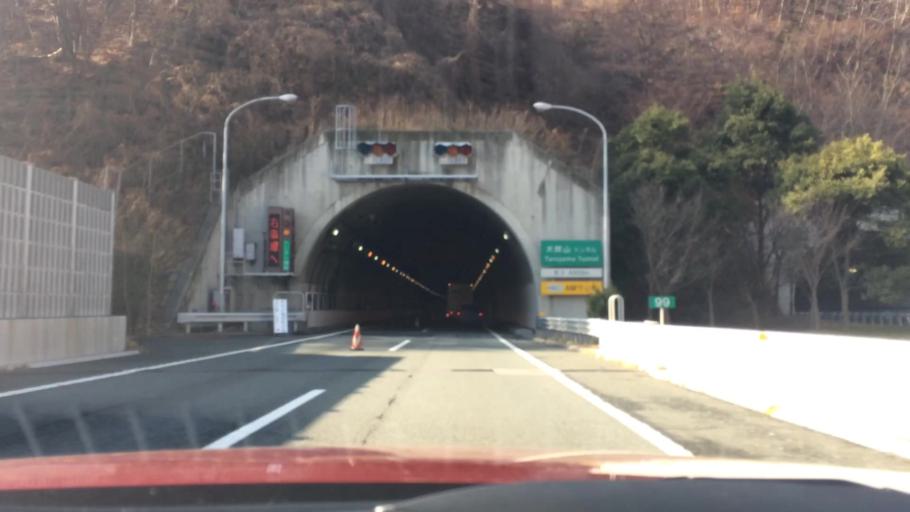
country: JP
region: Nagano
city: Ueda
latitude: 36.4228
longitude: 138.2632
